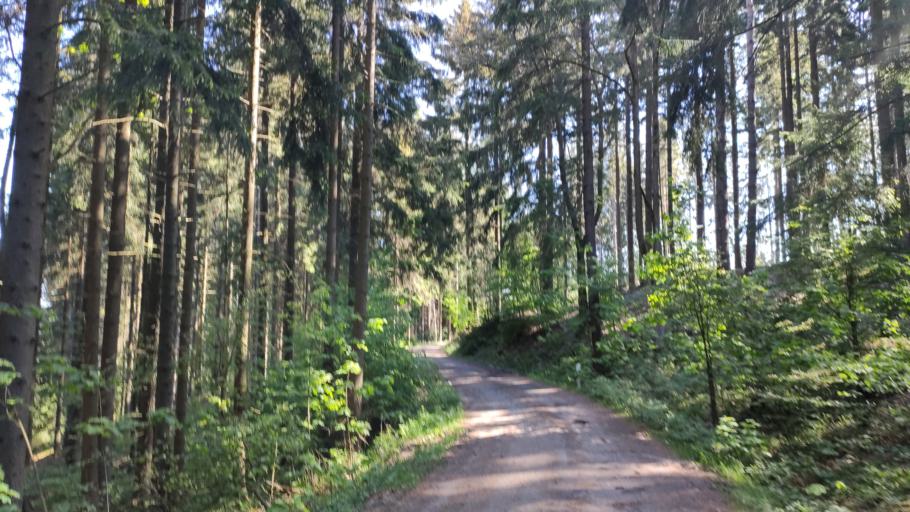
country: DE
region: Thuringia
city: Wurzbach
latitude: 50.4729
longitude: 11.4684
